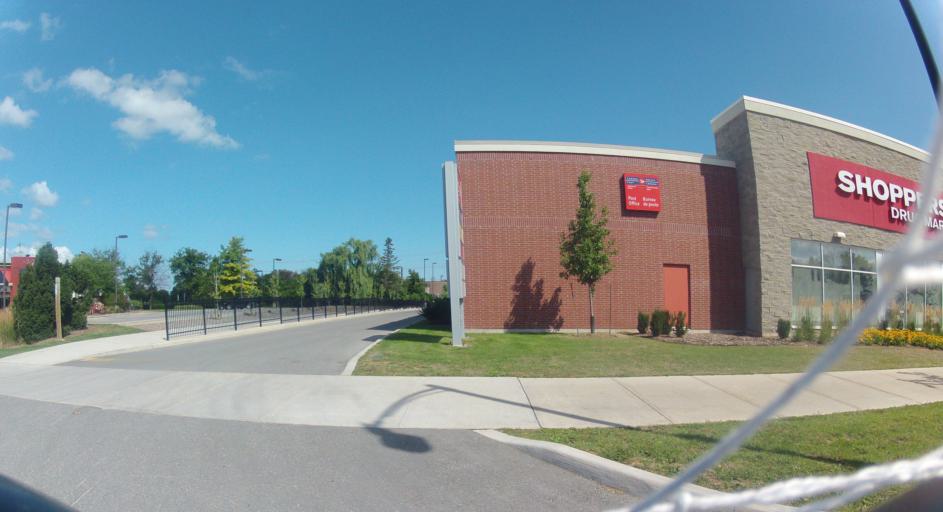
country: CA
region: Ontario
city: Collingwood
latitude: 44.5024
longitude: -80.2229
